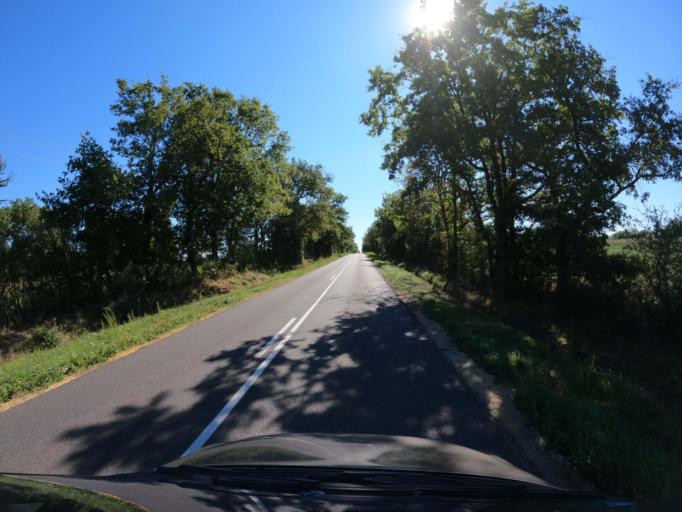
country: FR
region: Poitou-Charentes
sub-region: Departement de la Vienne
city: Saulge
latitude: 46.3939
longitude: 0.9038
